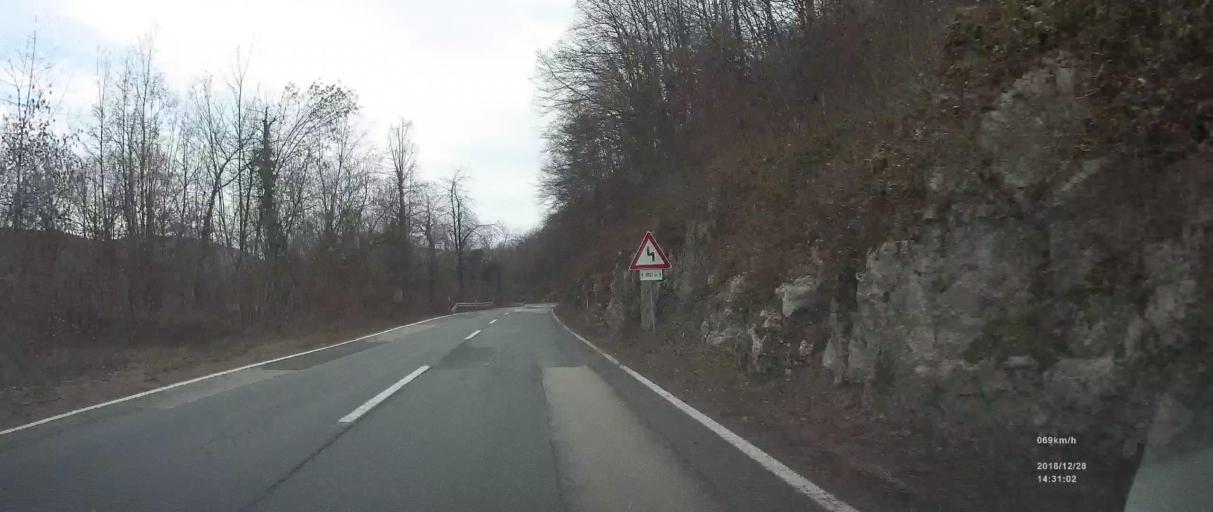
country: HR
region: Primorsko-Goranska
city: Vrbovsko
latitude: 45.4173
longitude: 15.1372
